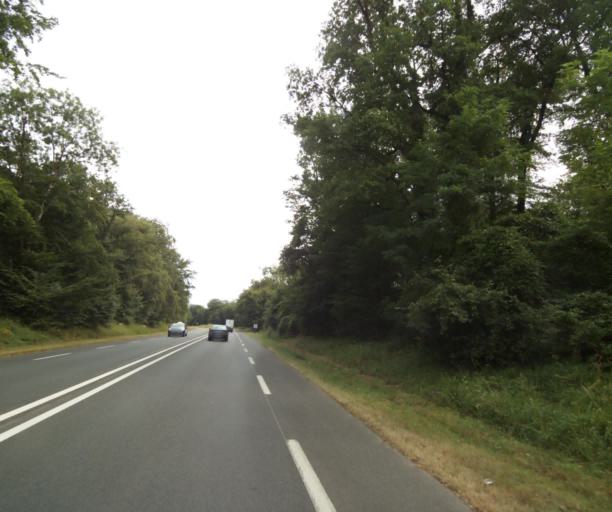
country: FR
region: Ile-de-France
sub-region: Departement de Seine-et-Marne
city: Fontainebleau
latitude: 48.4289
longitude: 2.7028
